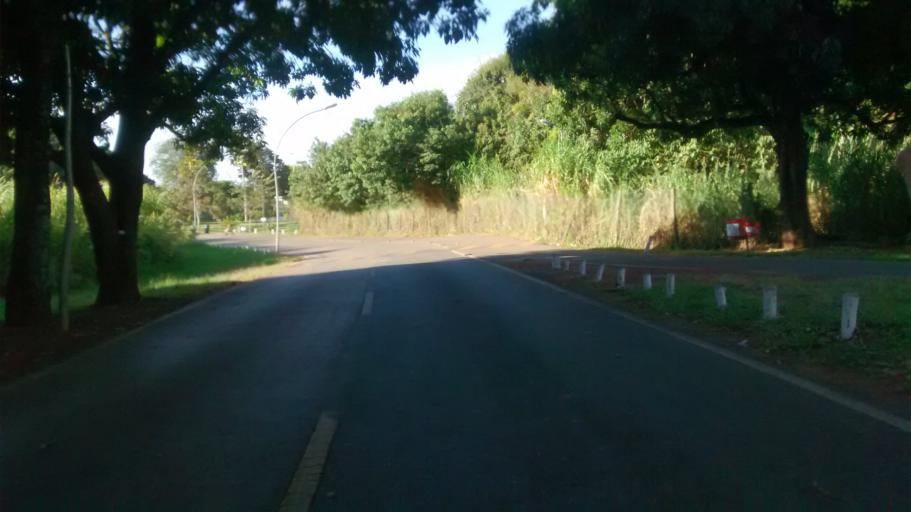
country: BR
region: Federal District
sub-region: Brasilia
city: Brasilia
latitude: -15.8312
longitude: -48.0224
